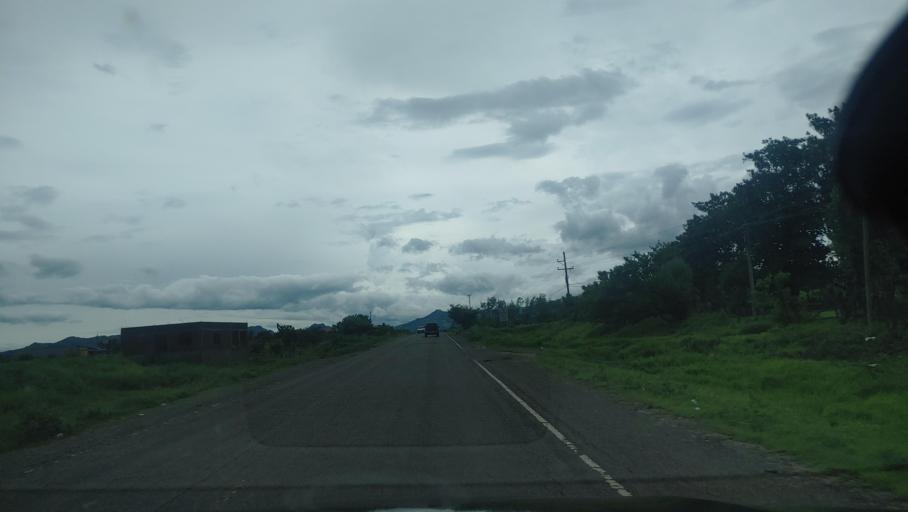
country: HN
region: Choluteca
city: Santa Ana de Yusguare
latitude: 13.3375
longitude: -87.1300
